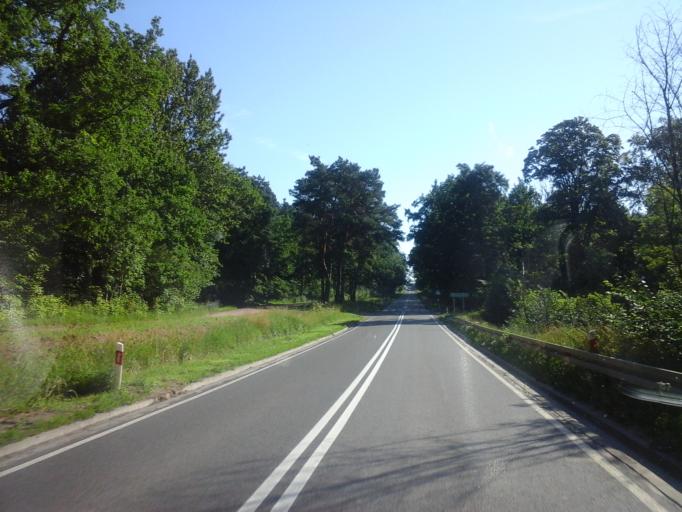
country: PL
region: West Pomeranian Voivodeship
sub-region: Powiat drawski
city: Drawsko Pomorskie
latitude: 53.4983
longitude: 15.7402
